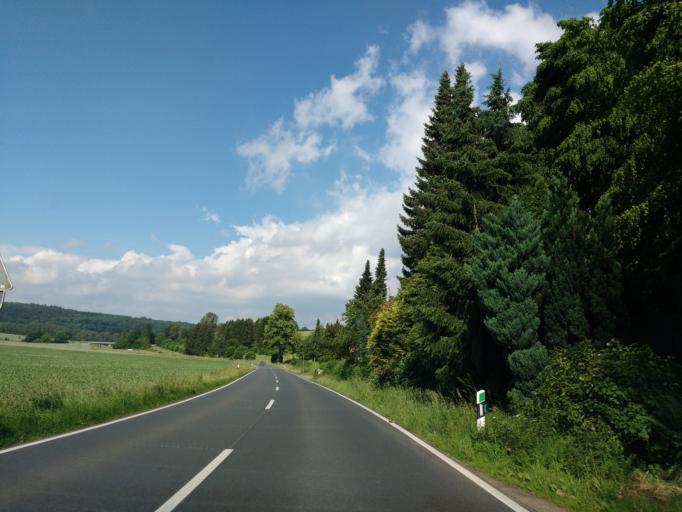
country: DE
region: North Rhine-Westphalia
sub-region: Regierungsbezirk Detmold
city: Vlotho
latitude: 52.1451
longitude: 8.9515
